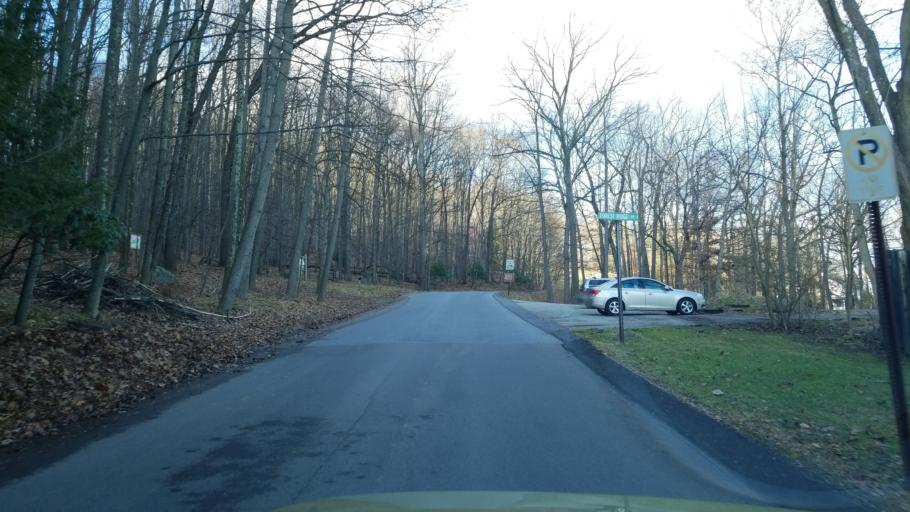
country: US
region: Pennsylvania
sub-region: Indiana County
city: Indiana
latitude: 40.6274
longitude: -79.1633
